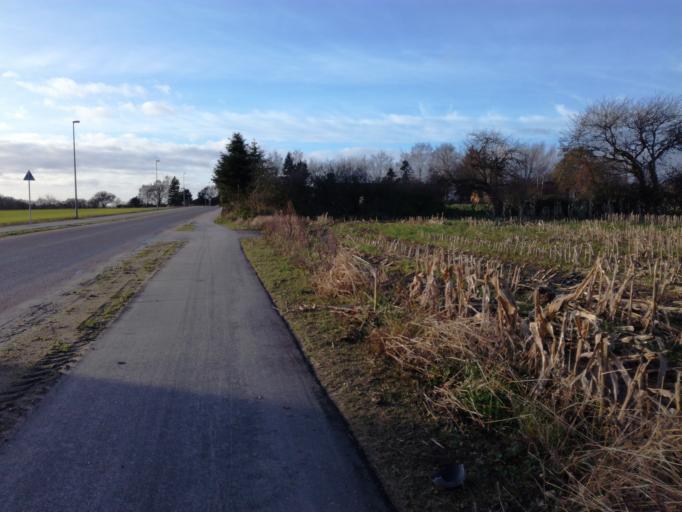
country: DK
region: South Denmark
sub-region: Fredericia Kommune
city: Fredericia
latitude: 55.6184
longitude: 9.7662
